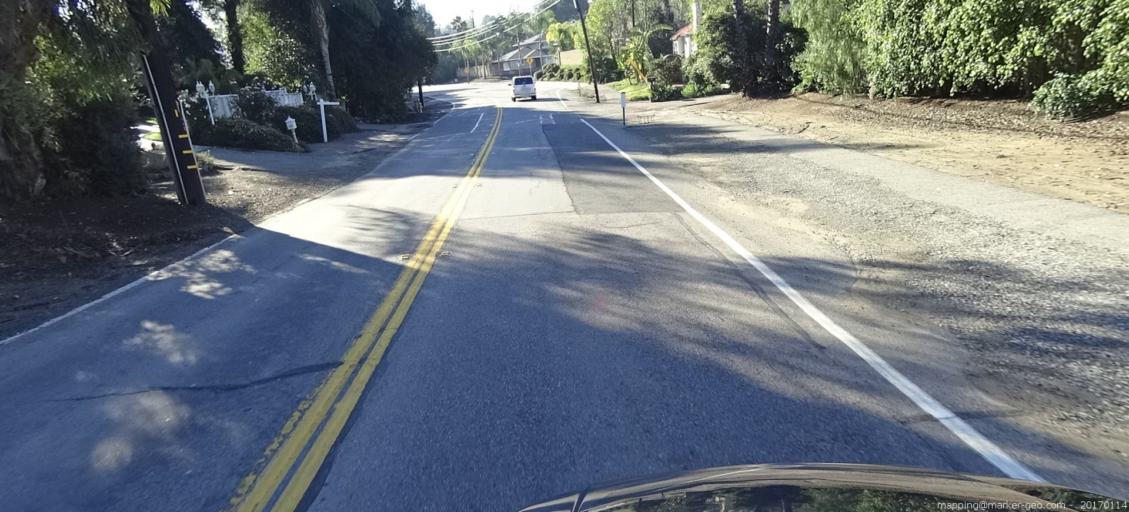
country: US
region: California
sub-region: Orange County
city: North Tustin
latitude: 33.7840
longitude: -117.7959
